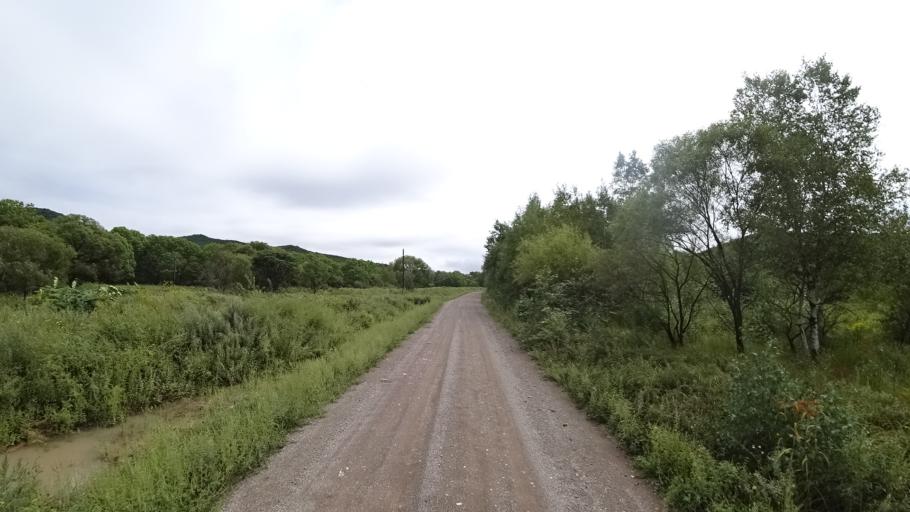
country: RU
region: Primorskiy
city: Monastyrishche
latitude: 44.1663
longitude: 132.5333
